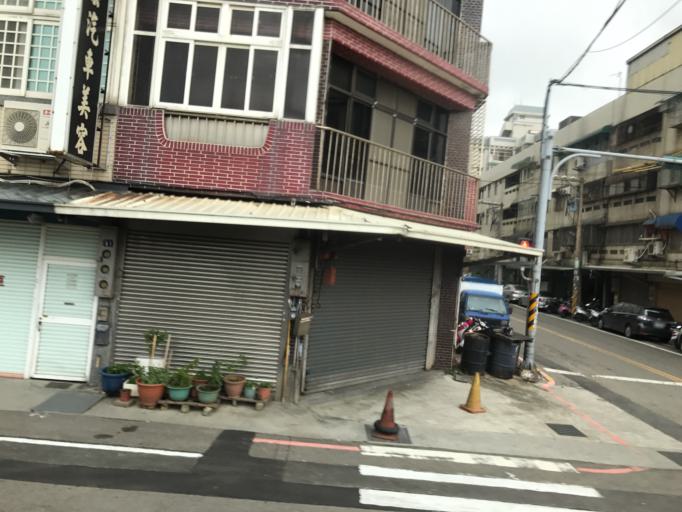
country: TW
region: Taiwan
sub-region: Hsinchu
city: Hsinchu
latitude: 24.8153
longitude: 120.9562
